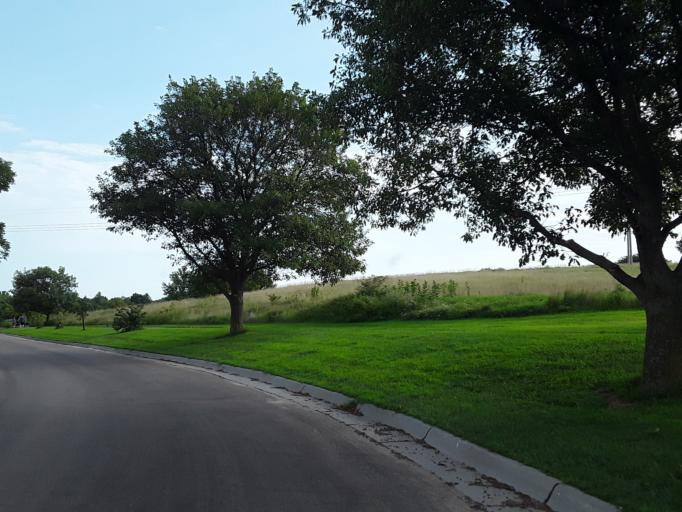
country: US
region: Nebraska
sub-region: Saunders County
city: Ashland
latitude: 41.0229
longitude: -96.3128
